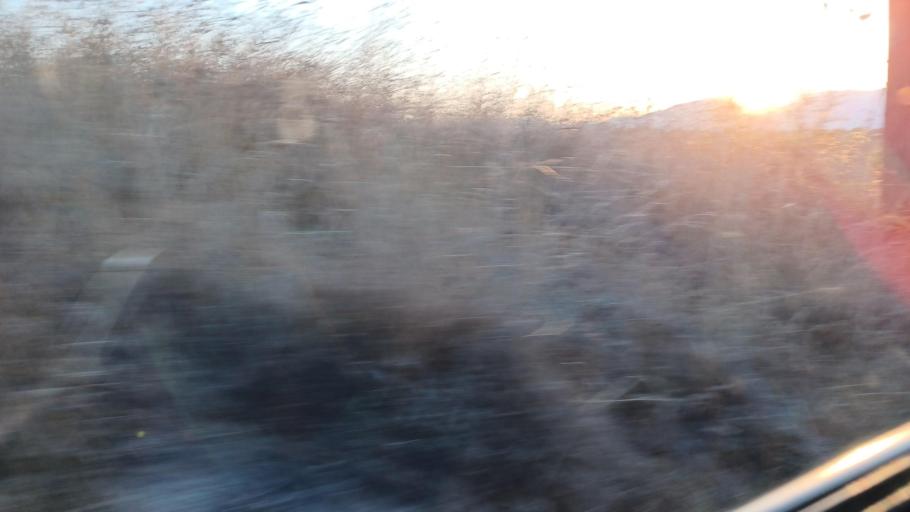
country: CY
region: Pafos
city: Mesogi
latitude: 34.8792
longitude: 32.5122
